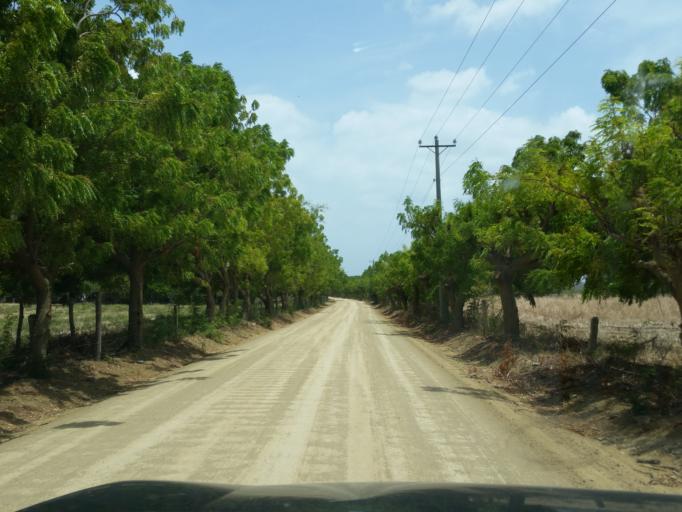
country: NI
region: Rivas
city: Tola
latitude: 11.4245
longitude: -86.0292
